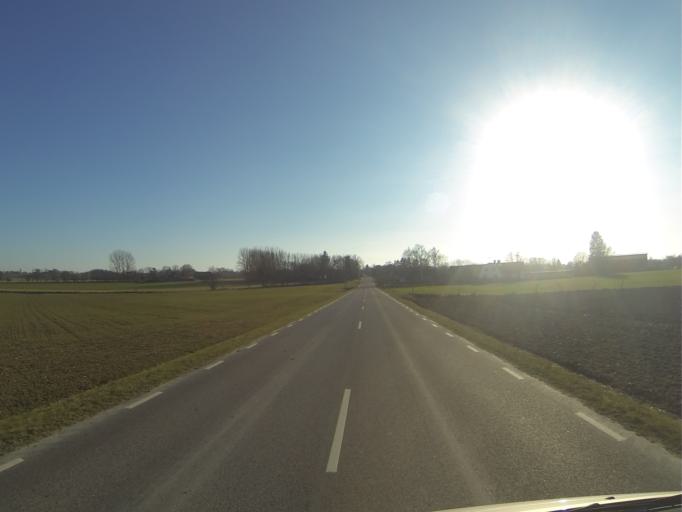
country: SE
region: Skane
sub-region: Horby Kommun
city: Hoerby
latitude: 55.8299
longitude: 13.6101
